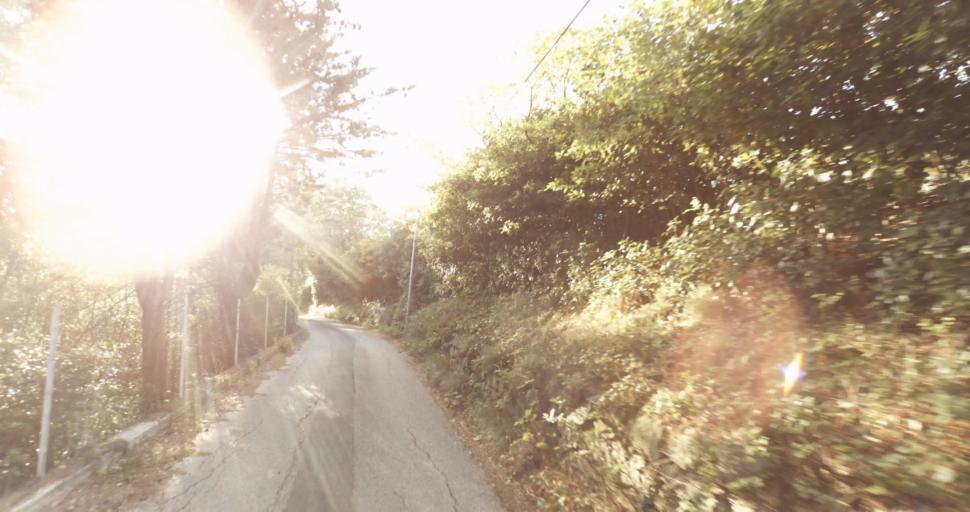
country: FR
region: Provence-Alpes-Cote d'Azur
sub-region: Departement des Bouches-du-Rhone
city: Venelles
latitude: 43.6243
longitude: 5.4652
